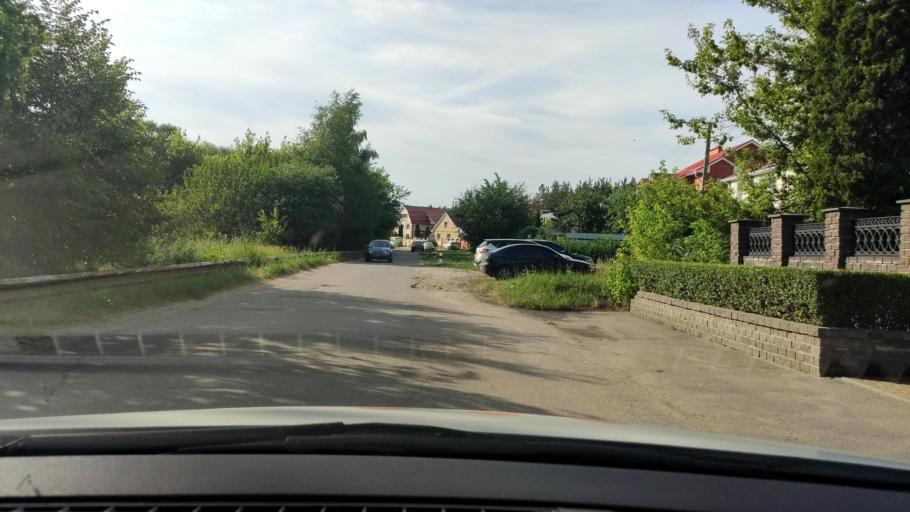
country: RU
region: Voronezj
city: Novaya Usman'
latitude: 51.6275
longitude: 39.4222
